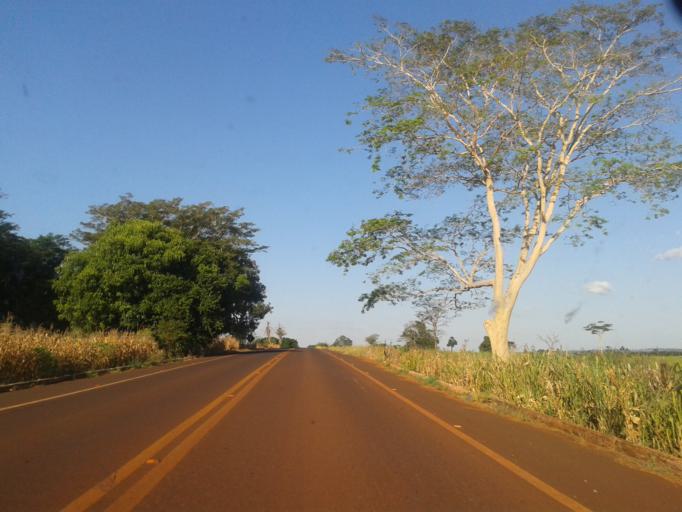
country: BR
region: Minas Gerais
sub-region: Santa Vitoria
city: Santa Vitoria
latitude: -18.6913
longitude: -49.9012
